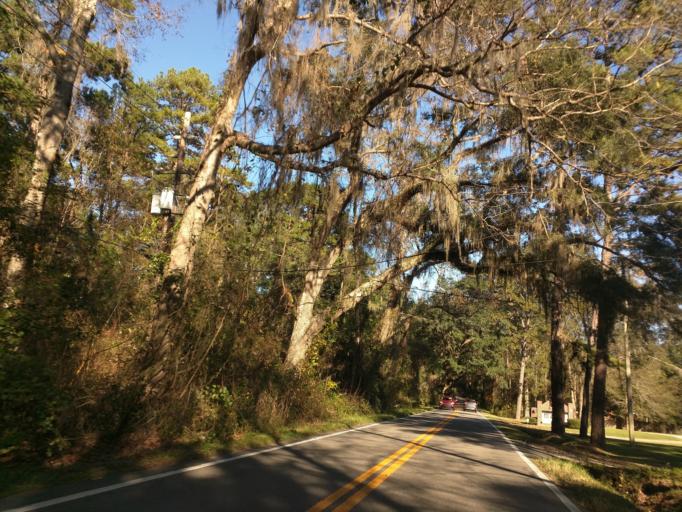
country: US
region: Florida
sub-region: Leon County
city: Tallahassee
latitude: 30.4783
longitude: -84.2135
